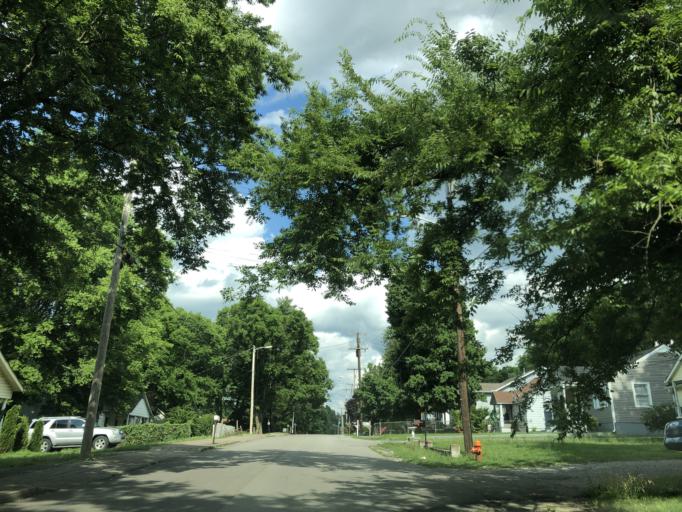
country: US
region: Tennessee
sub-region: Davidson County
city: Nashville
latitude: 36.2083
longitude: -86.7647
